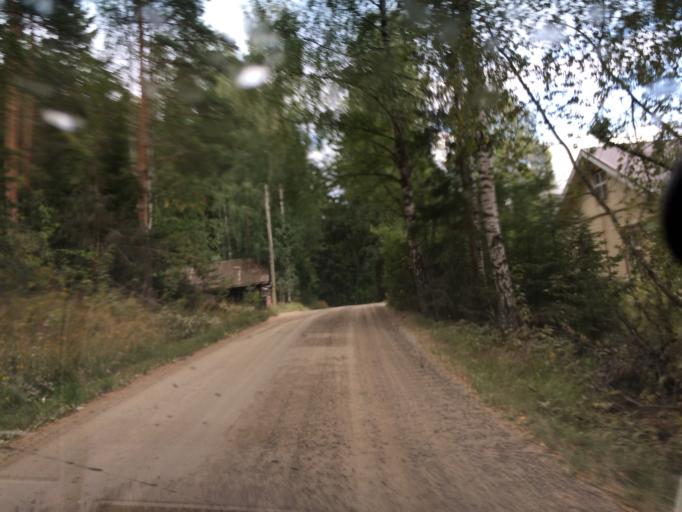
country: FI
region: Pirkanmaa
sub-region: Tampere
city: Luopioinen
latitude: 61.2677
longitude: 24.6854
